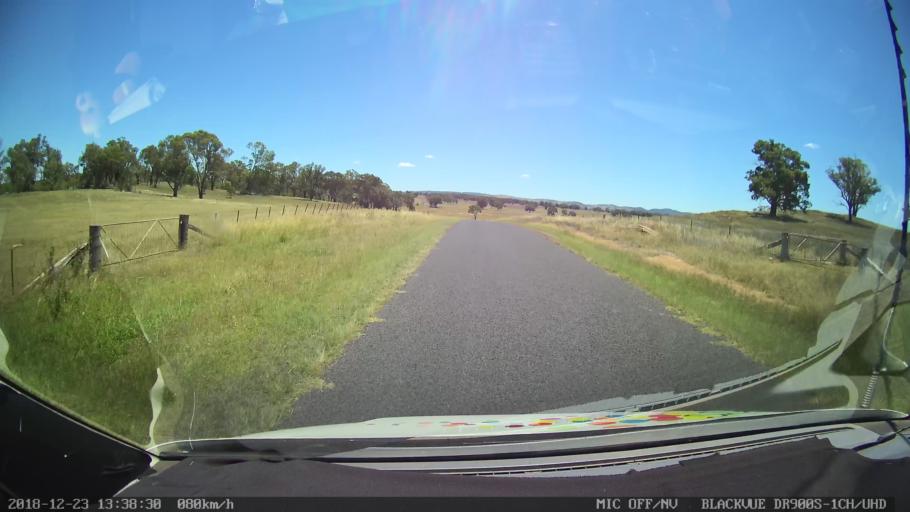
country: AU
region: New South Wales
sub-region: Armidale Dumaresq
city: Armidale
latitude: -30.4511
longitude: 151.2121
